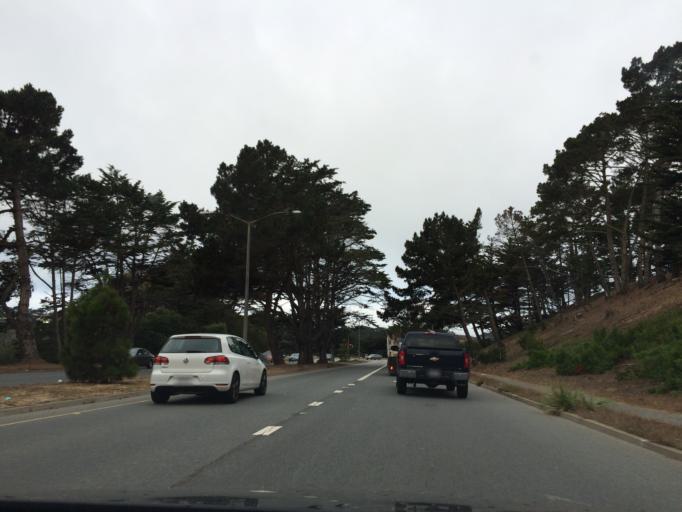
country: US
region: California
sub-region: San Mateo County
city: Daly City
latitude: 37.7147
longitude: -122.4833
